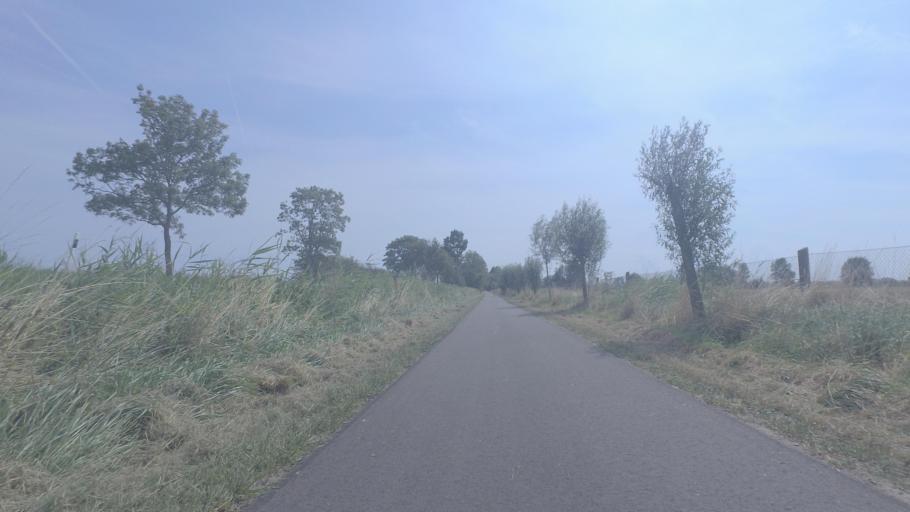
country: DE
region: Mecklenburg-Vorpommern
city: Garz
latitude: 54.2668
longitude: 13.3476
